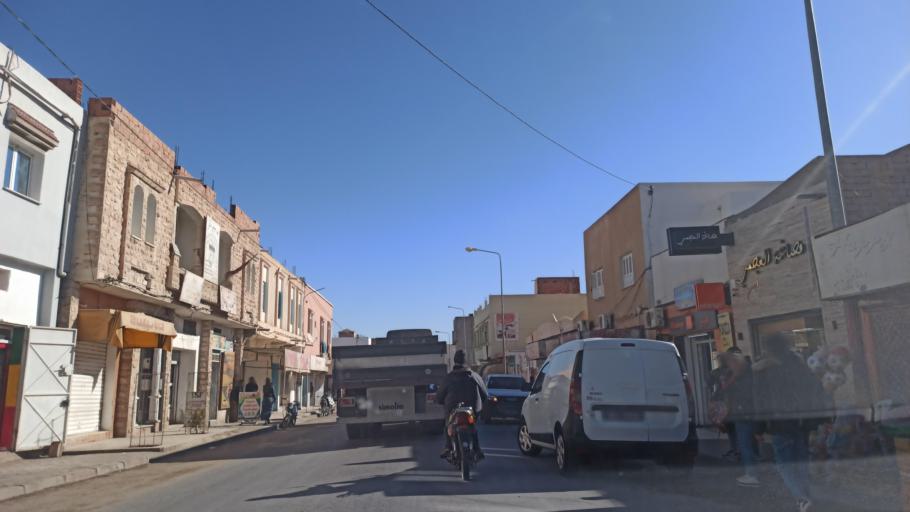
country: TN
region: Gafsa
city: Al Metlaoui
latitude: 34.3151
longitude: 8.4061
